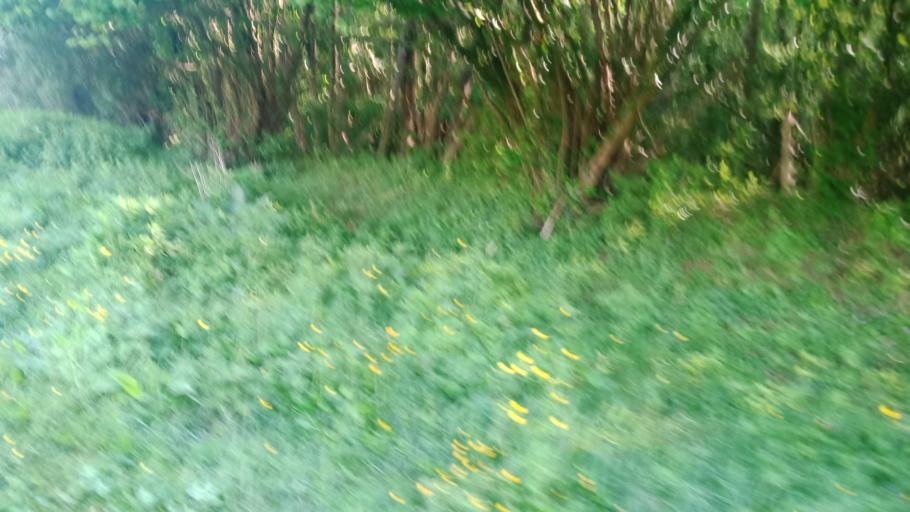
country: FR
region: Rhone-Alpes
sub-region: Departement de l'Isere
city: Serpaize
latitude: 45.5474
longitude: 4.9407
